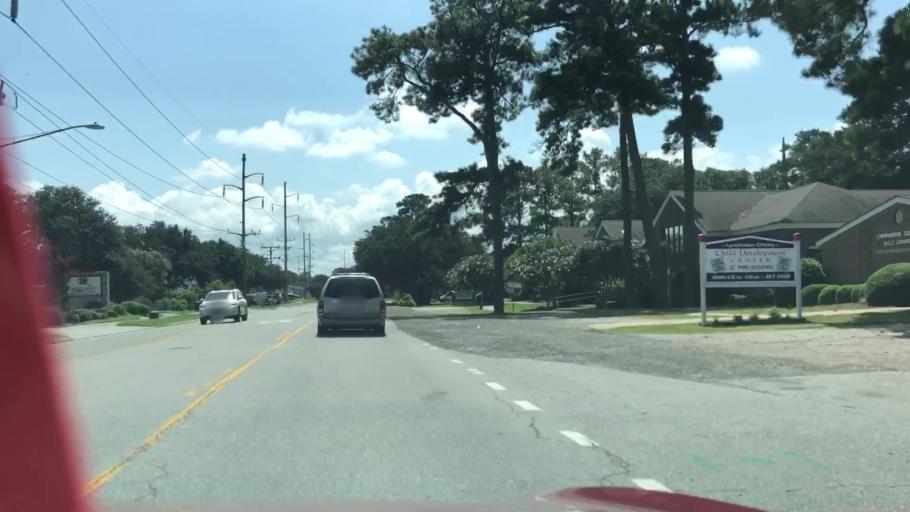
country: US
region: Virginia
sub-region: City of Virginia Beach
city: Virginia Beach
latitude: 36.9091
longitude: -76.0707
